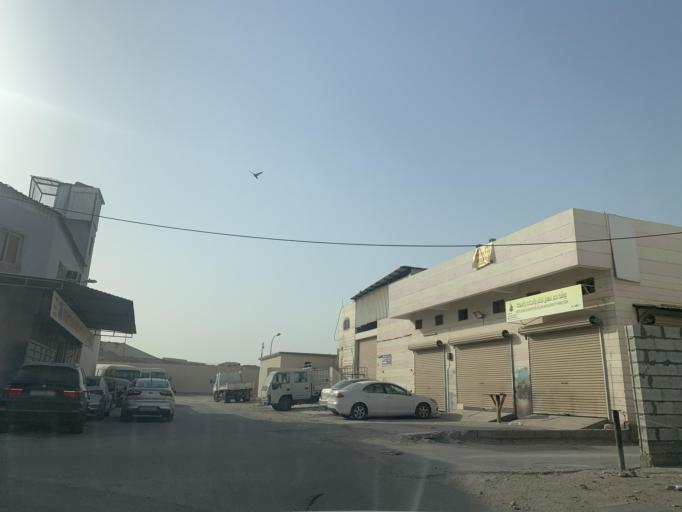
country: BH
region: Central Governorate
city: Madinat Hamad
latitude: 26.1469
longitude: 50.4843
